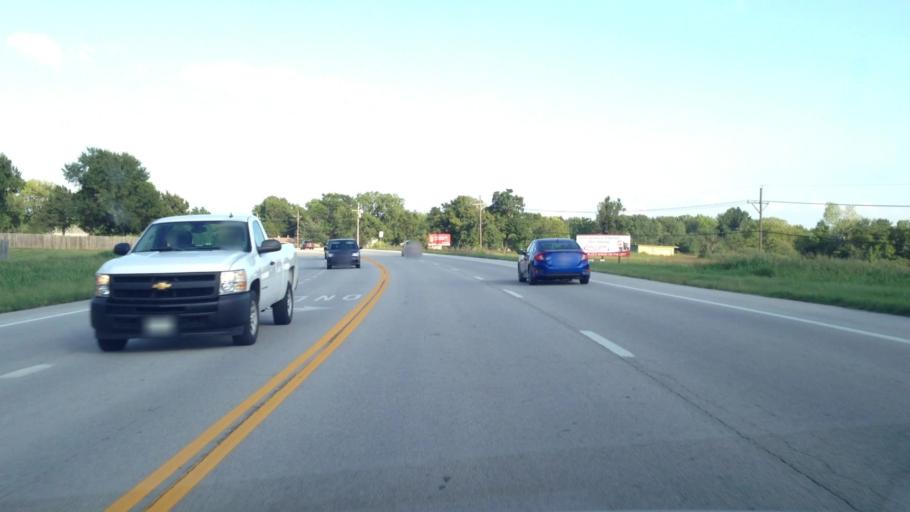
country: US
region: Missouri
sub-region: Jasper County
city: Carl Junction
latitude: 37.1434
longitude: -94.5198
